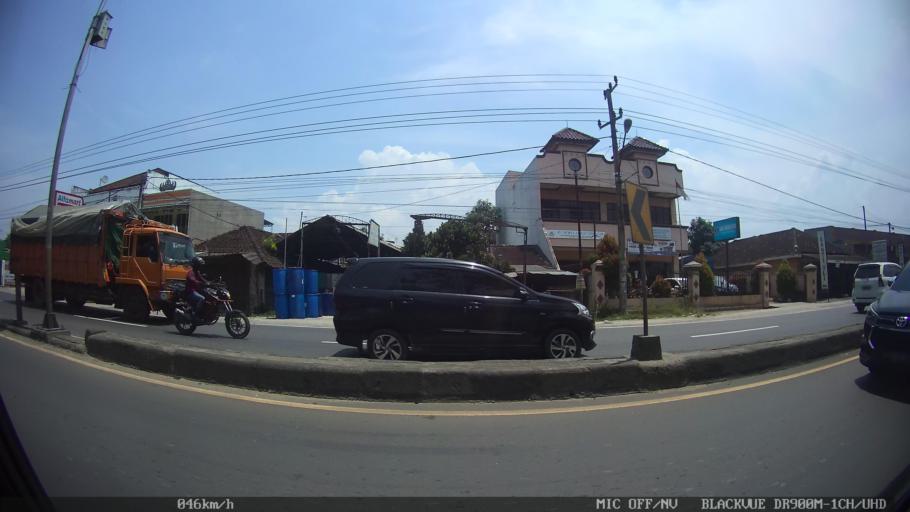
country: ID
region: Lampung
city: Natar
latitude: -5.3272
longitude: 105.2018
